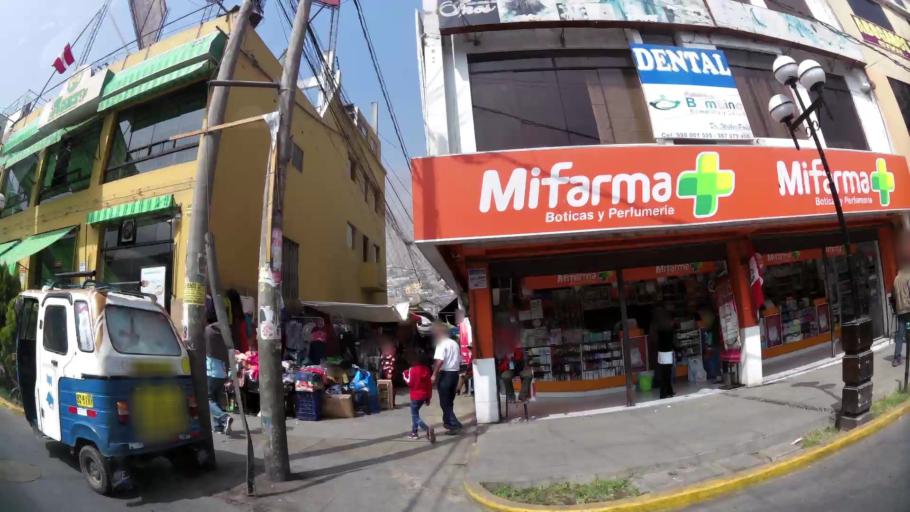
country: PE
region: Lima
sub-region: Lima
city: Asentamiento Humano Nicolas de Pierola
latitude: -11.9355
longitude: -76.6938
